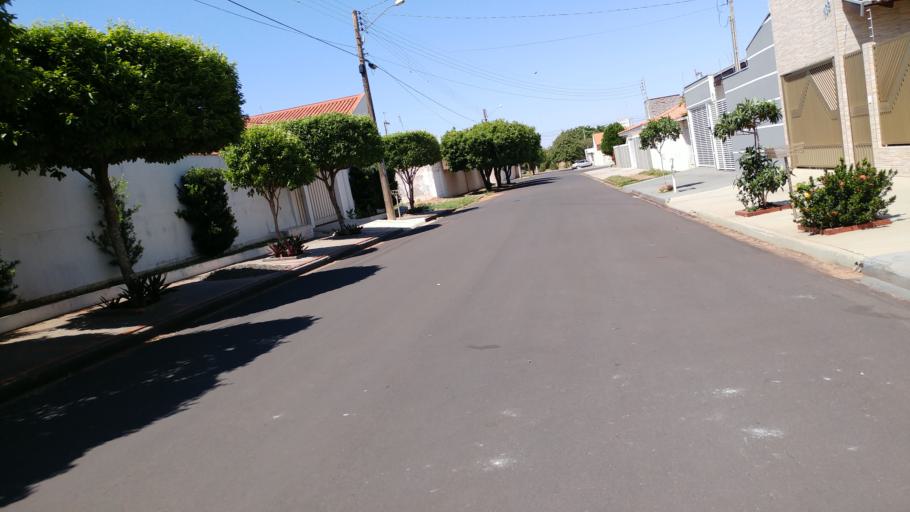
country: BR
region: Sao Paulo
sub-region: Paraguacu Paulista
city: Paraguacu Paulista
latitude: -22.4097
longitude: -50.5872
